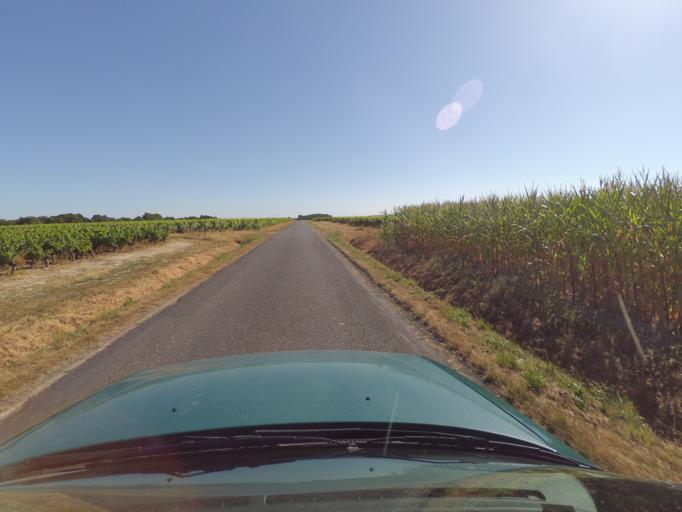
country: FR
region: Pays de la Loire
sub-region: Departement de la Loire-Atlantique
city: Maisdon-sur-Sevre
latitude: 47.0889
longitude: -1.3711
